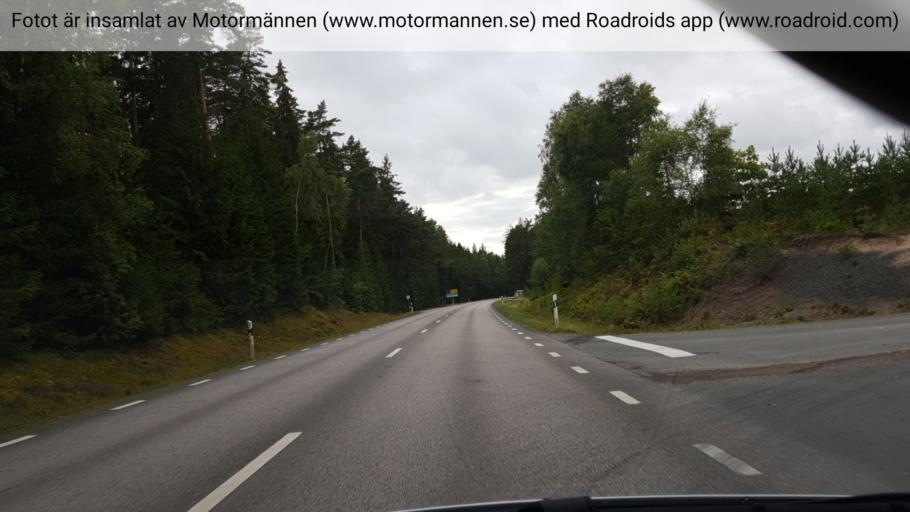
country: SE
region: Vaestra Goetaland
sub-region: Tibro Kommun
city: Tibro
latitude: 58.3429
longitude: 14.1587
